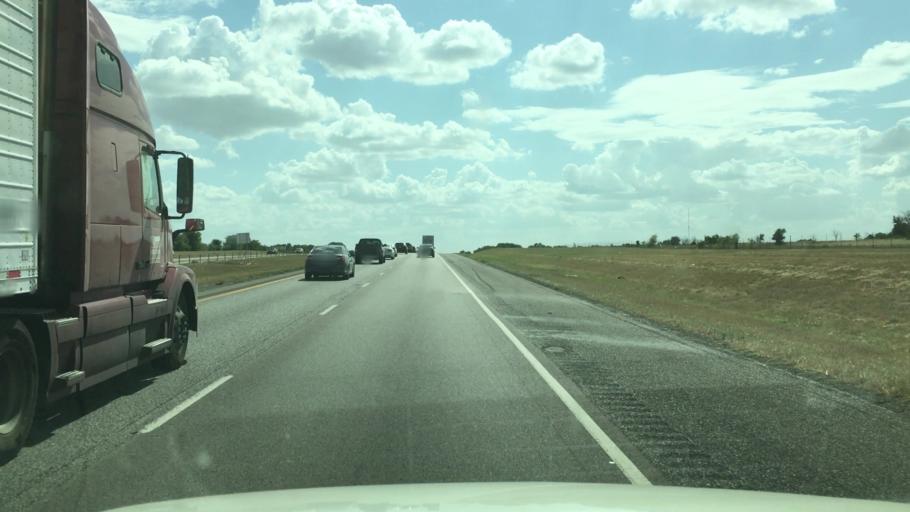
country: US
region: Texas
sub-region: Ellis County
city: Plum Grove
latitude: 32.1140
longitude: -96.9934
